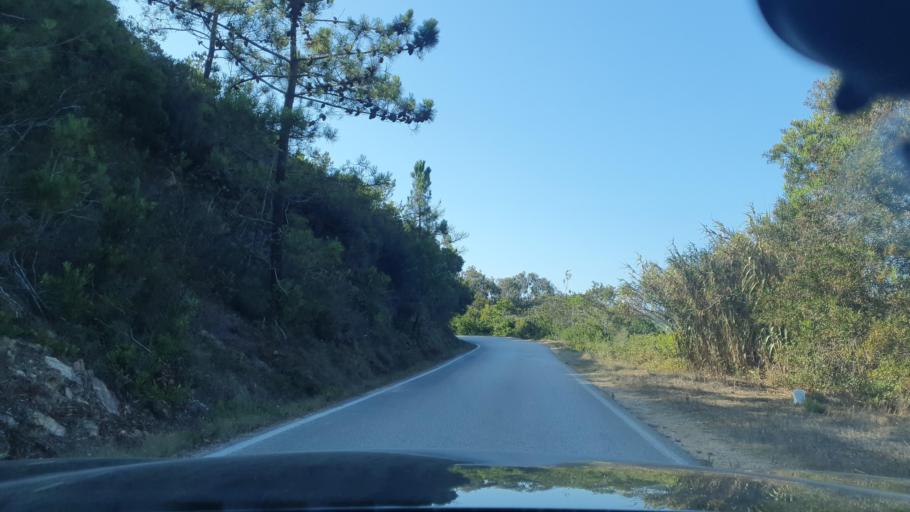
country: PT
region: Beja
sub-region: Odemira
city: Sao Teotonio
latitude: 37.4351
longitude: -8.7932
